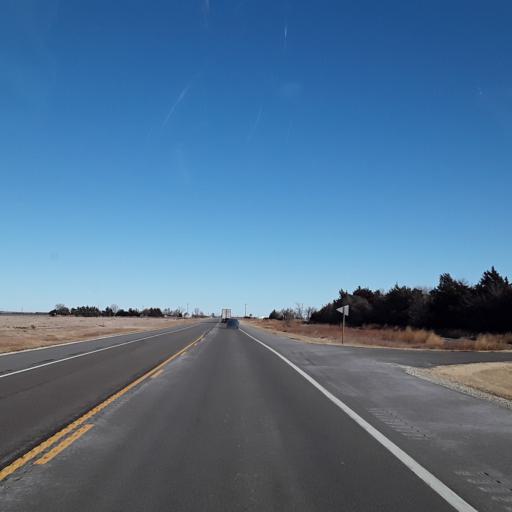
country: US
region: Kansas
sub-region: Pawnee County
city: Larned
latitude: 38.1913
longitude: -99.0809
